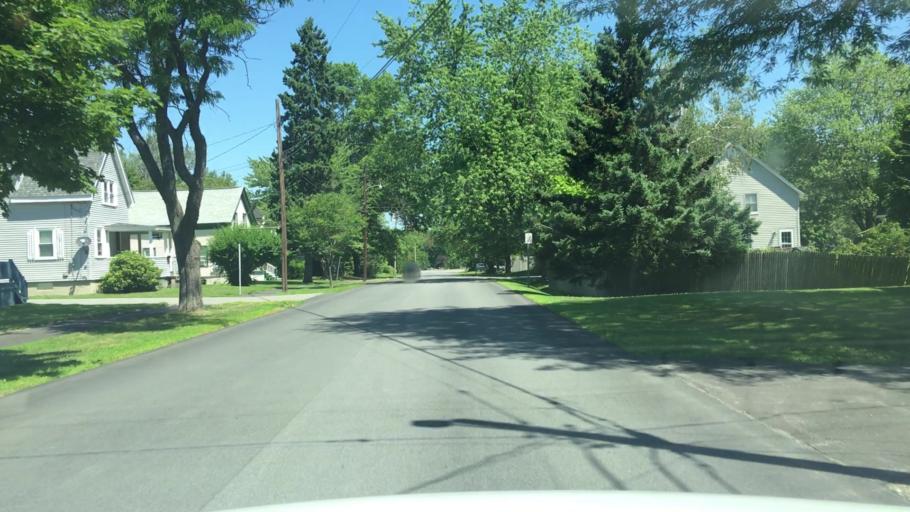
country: US
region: Maine
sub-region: Penobscot County
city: Bangor
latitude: 44.8112
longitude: -68.7952
